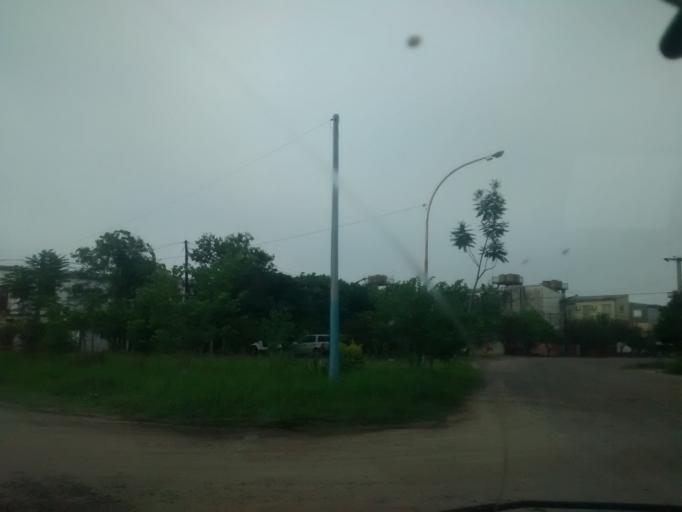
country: AR
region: Chaco
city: Resistencia
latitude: -27.4681
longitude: -58.9834
